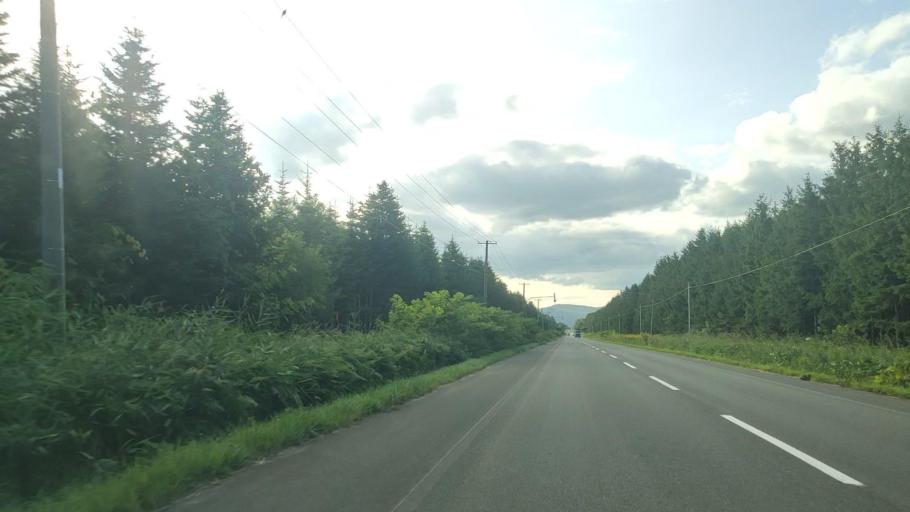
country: JP
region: Hokkaido
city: Makubetsu
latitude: 44.8870
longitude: 142.0080
